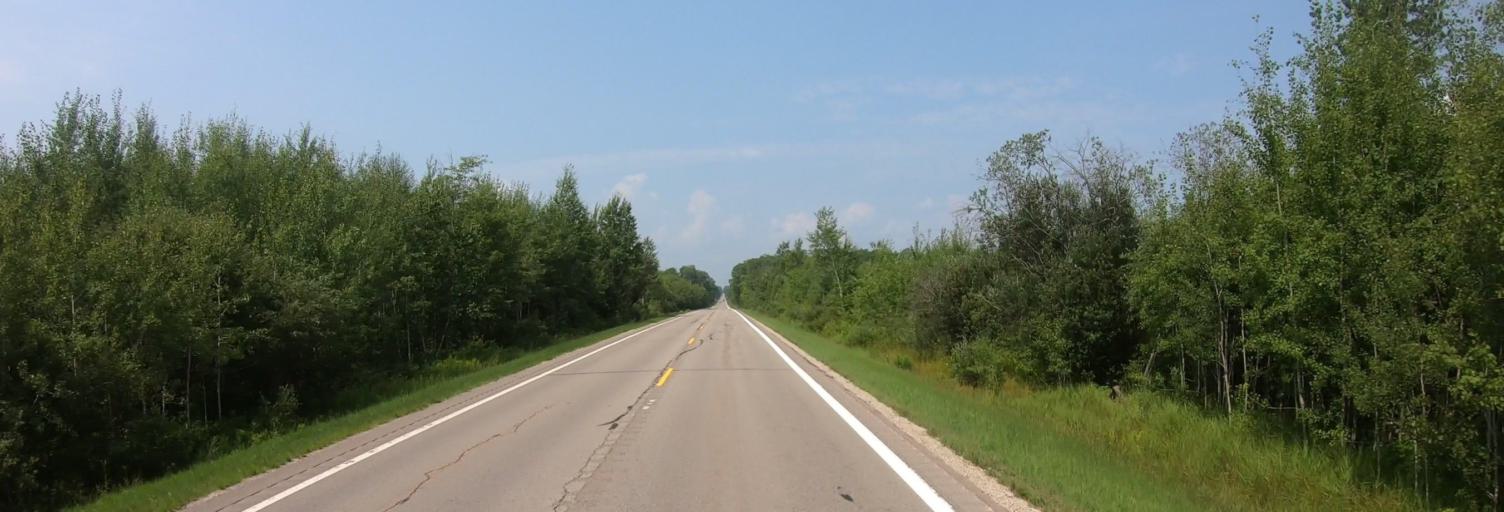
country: US
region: Michigan
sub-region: Luce County
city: Newberry
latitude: 46.5641
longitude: -85.3075
